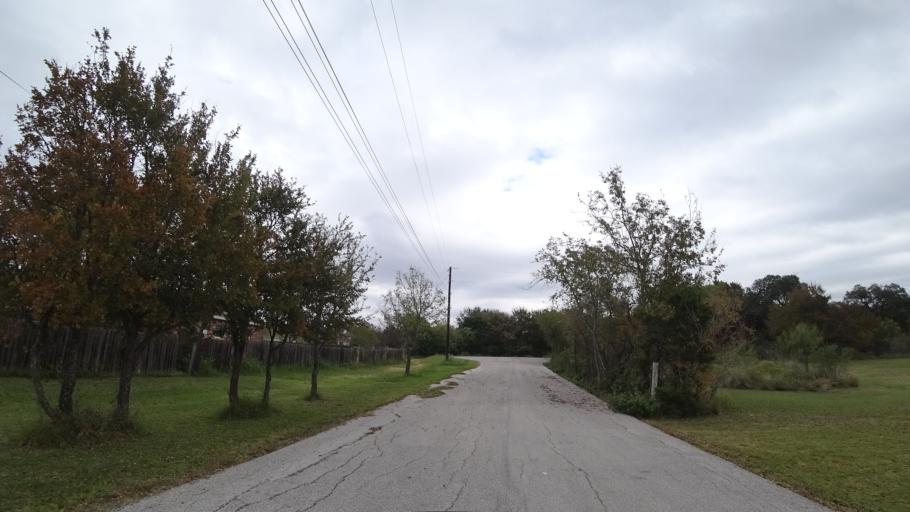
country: US
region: Texas
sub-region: Travis County
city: Shady Hollow
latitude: 30.1493
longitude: -97.8602
